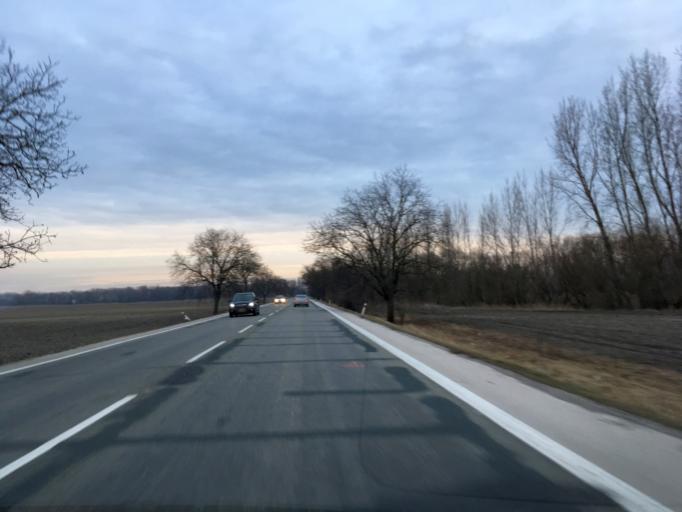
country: SK
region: Trnavsky
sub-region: Okres Dunajska Streda
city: Velky Meder
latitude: 47.9074
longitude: 17.7365
